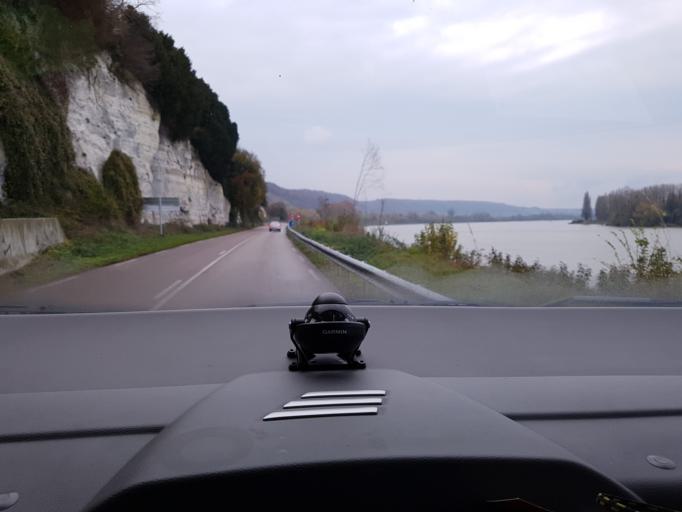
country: FR
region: Haute-Normandie
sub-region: Departement de la Seine-Maritime
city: Saint-Pierre-de-Varengeville
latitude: 49.4861
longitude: 0.9119
